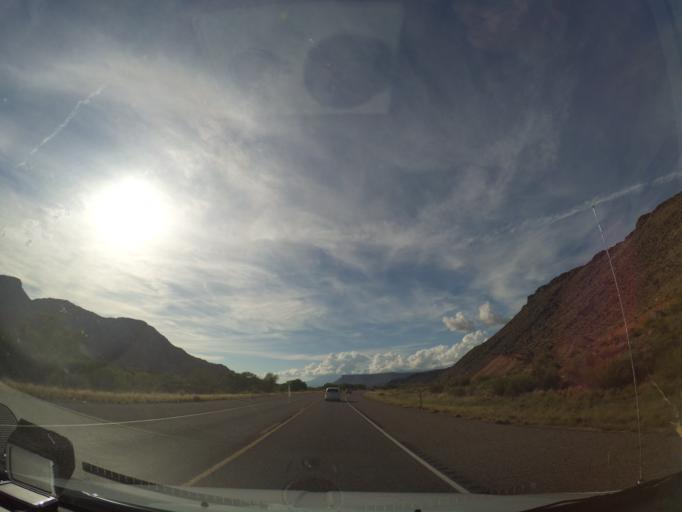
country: US
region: Utah
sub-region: Washington County
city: LaVerkin
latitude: 37.1826
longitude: -113.1331
